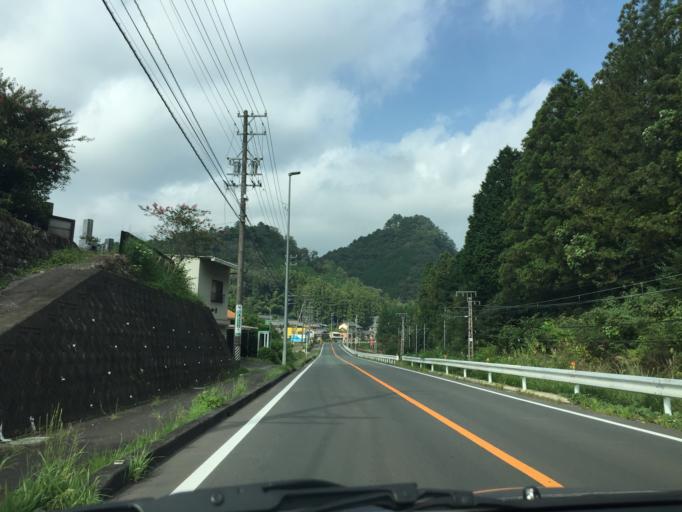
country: JP
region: Aichi
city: Shinshiro
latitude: 34.9367
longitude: 137.5880
